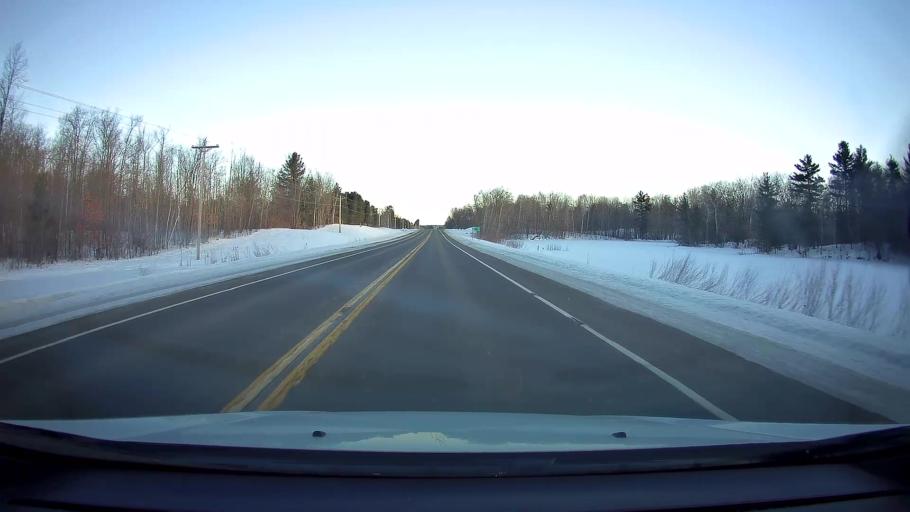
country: US
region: Wisconsin
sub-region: Barron County
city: Cumberland
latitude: 45.5862
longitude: -92.0176
